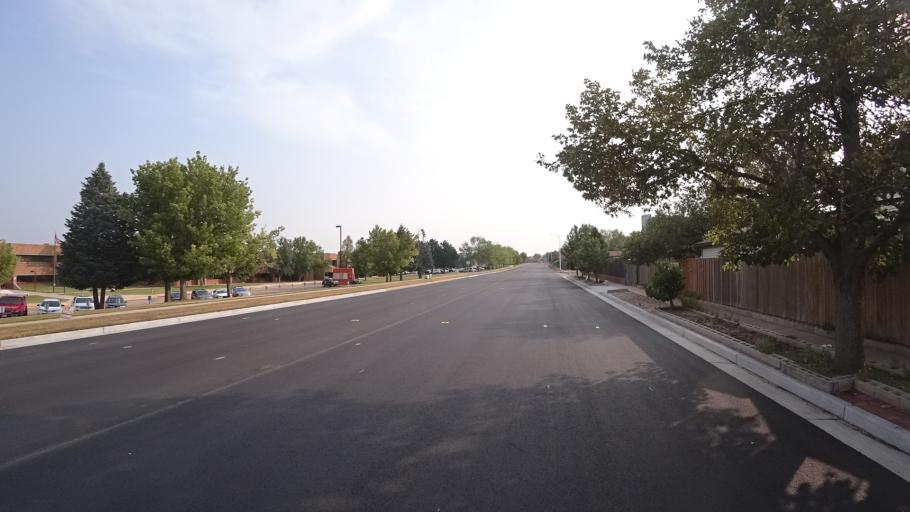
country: US
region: Colorado
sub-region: El Paso County
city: Stratmoor
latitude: 38.8007
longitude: -104.7522
